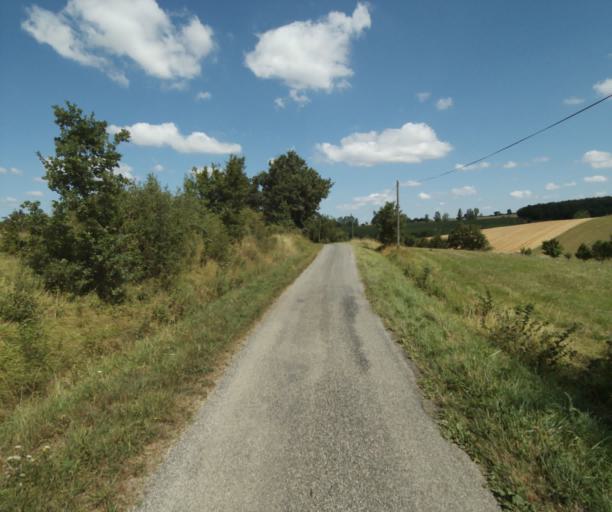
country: FR
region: Midi-Pyrenees
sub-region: Departement de la Haute-Garonne
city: Auriac-sur-Vendinelle
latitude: 43.4774
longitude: 1.7965
